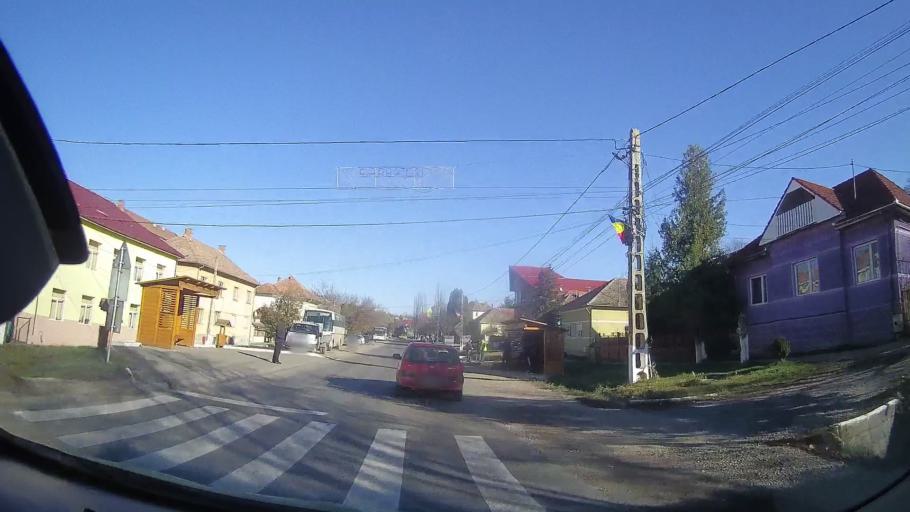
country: RO
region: Mures
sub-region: Comuna Sarmasu
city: Sarmasu
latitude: 46.7514
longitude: 24.1583
